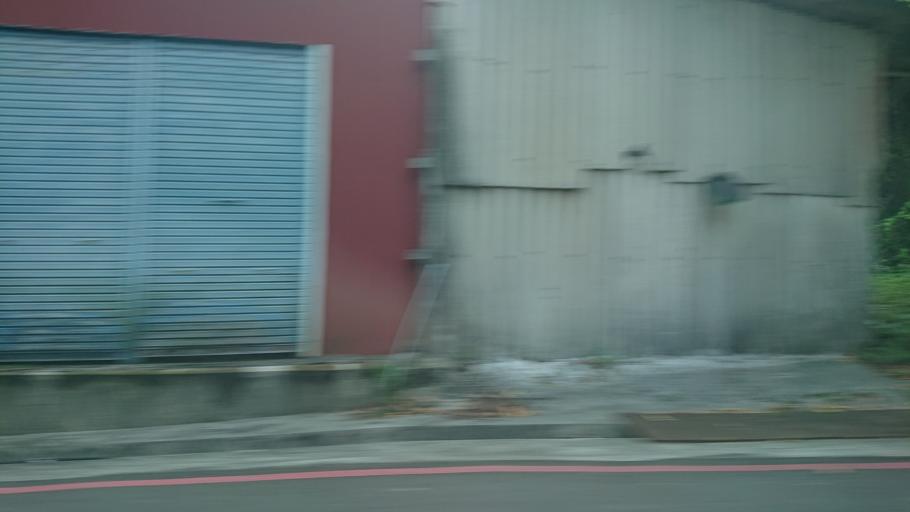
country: TW
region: Taiwan
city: Daxi
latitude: 24.8660
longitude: 121.4160
